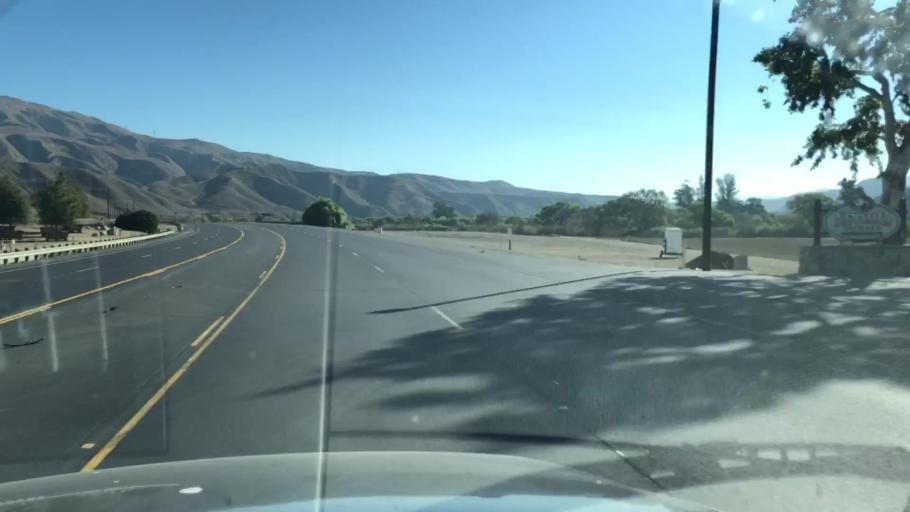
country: US
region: California
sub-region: Ventura County
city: Piru
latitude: 34.4060
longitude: -118.7405
